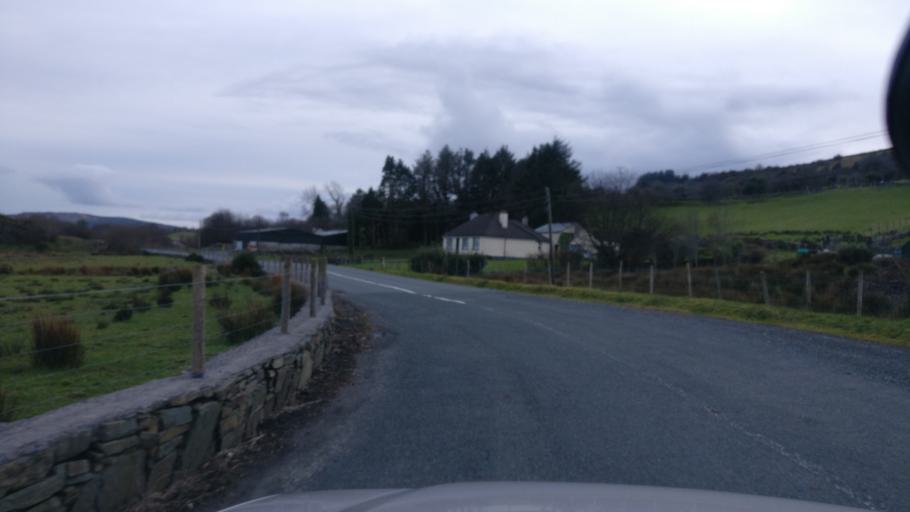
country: IE
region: Connaught
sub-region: County Galway
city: Oughterard
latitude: 53.5324
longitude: -9.4646
